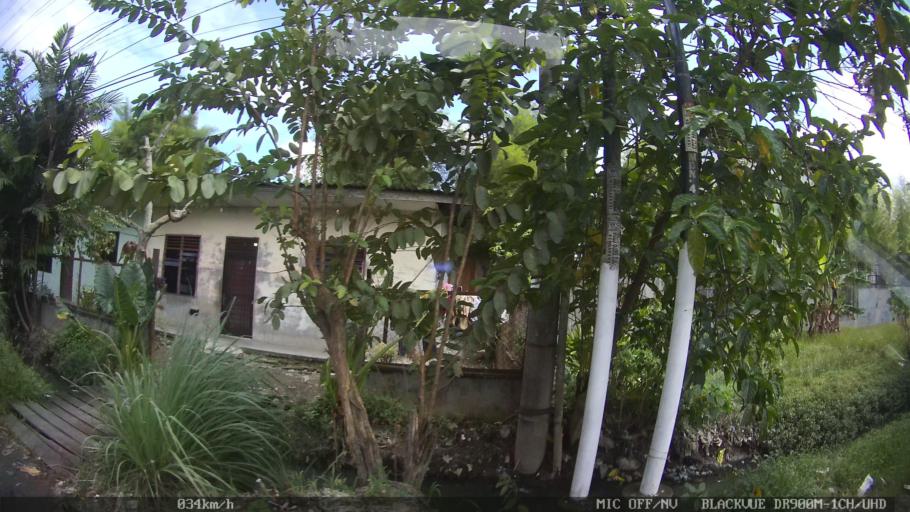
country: ID
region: North Sumatra
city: Percut
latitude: 3.6021
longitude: 98.7723
